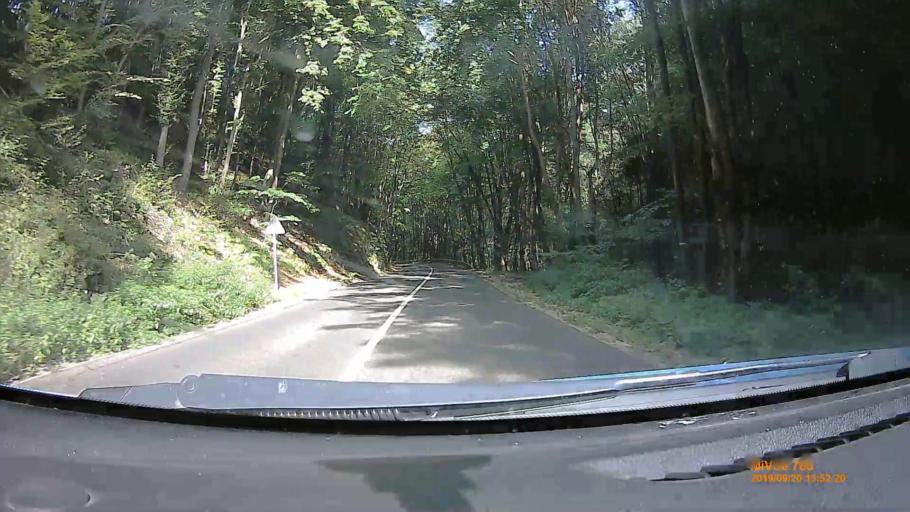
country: HU
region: Borsod-Abauj-Zemplen
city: Saly
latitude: 48.0715
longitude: 20.6037
